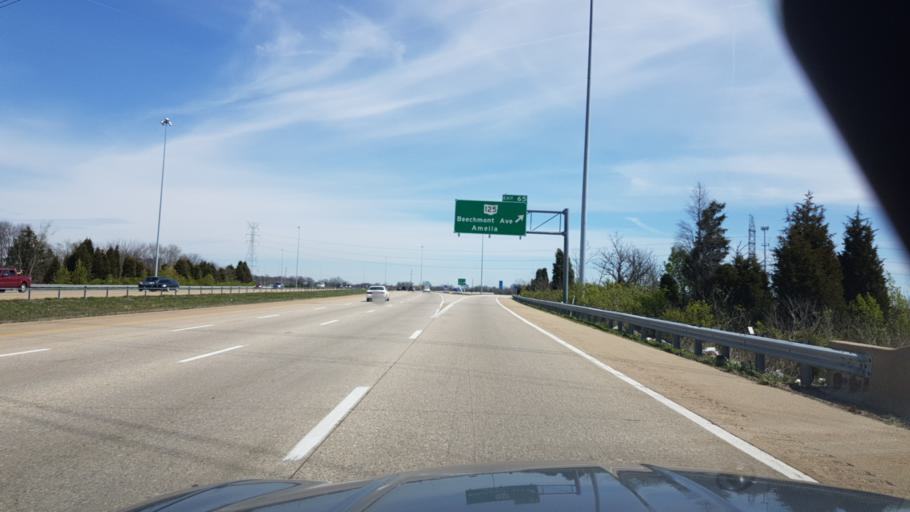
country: US
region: Ohio
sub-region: Clermont County
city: Withamsville
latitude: 39.0652
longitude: -84.3044
